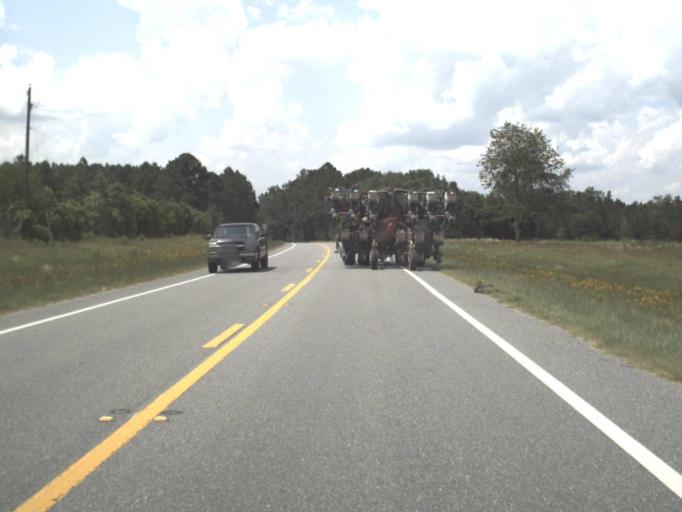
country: US
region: Georgia
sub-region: Echols County
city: Statenville
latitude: 30.5935
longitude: -83.0937
